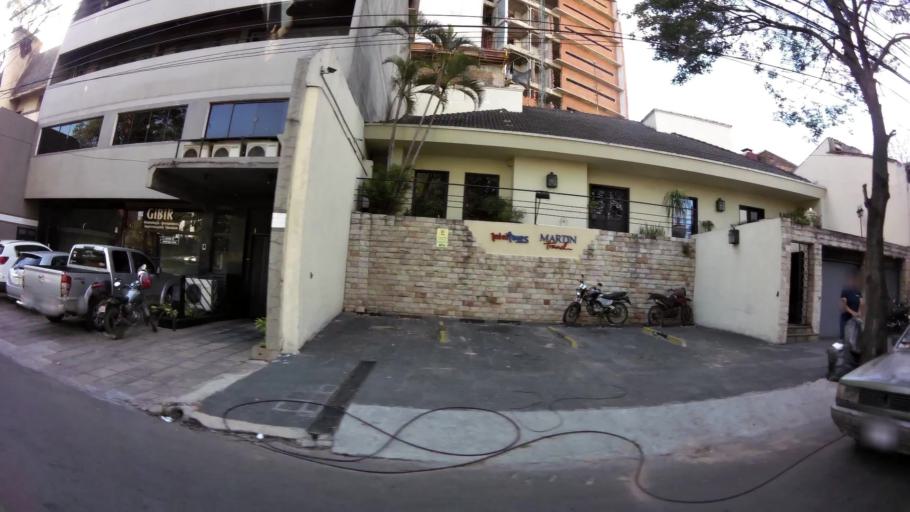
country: PY
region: Asuncion
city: Asuncion
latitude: -25.2867
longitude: -57.6169
